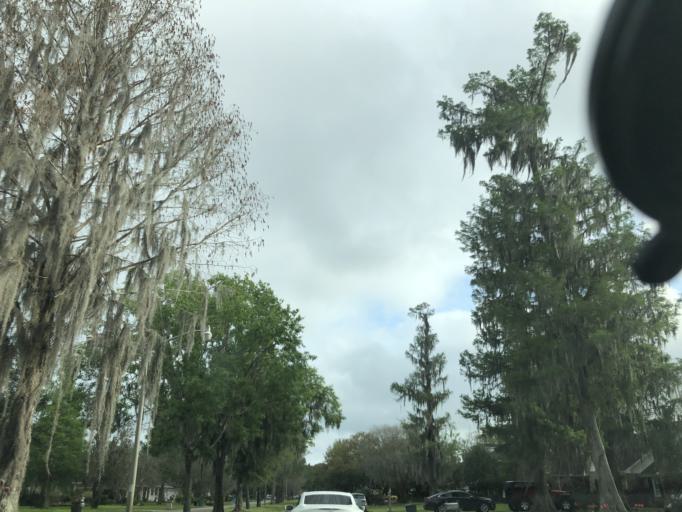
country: US
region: Louisiana
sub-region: Saint Charles Parish
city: New Sarpy
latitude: 29.9775
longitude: -90.3639
